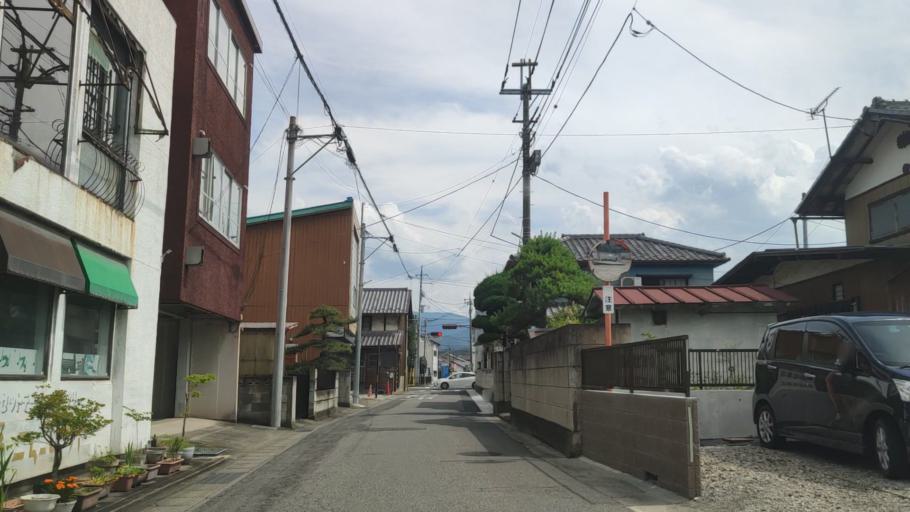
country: JP
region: Gunma
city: Tomioka
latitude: 36.2584
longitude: 138.8929
